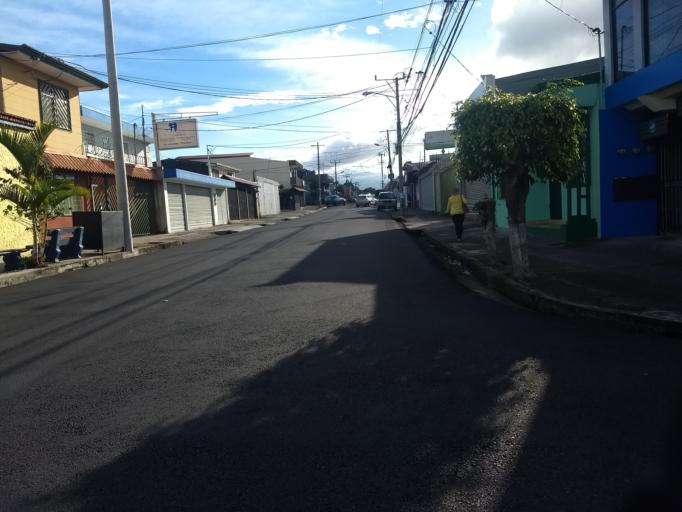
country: CR
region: San Jose
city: San Juan
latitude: 9.9588
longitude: -84.0794
